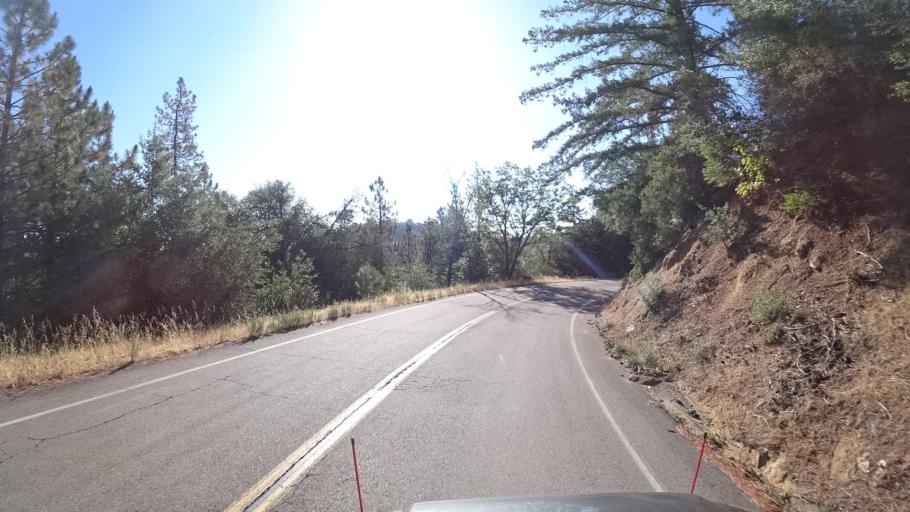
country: US
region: California
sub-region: Riverside County
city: Aguanga
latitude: 33.2858
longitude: -116.7943
